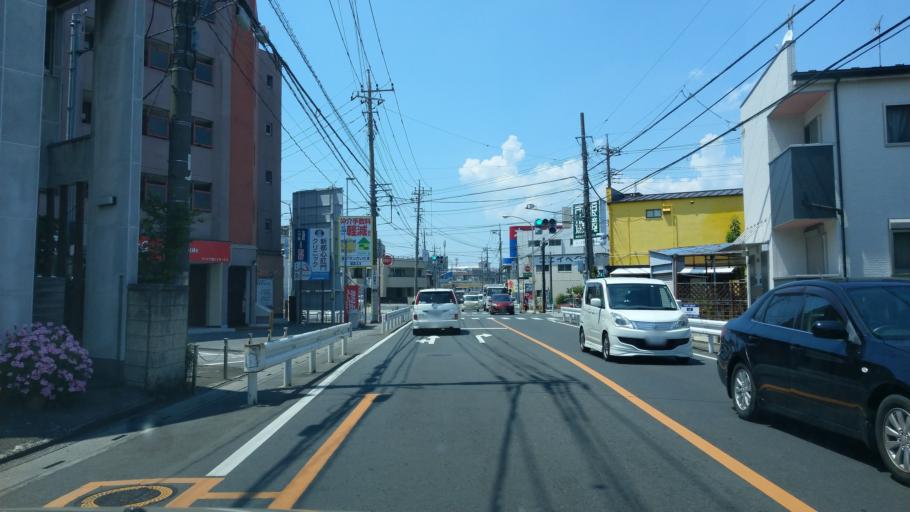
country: JP
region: Saitama
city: Yono
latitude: 35.8862
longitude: 139.6471
